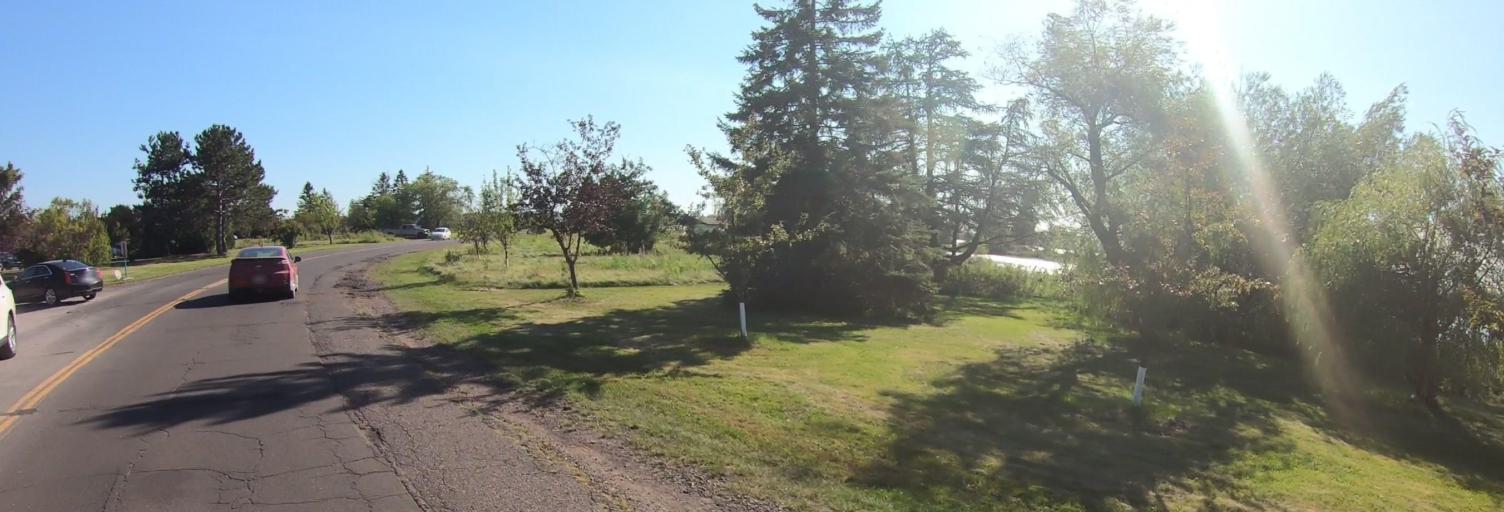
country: US
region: Wisconsin
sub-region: Douglas County
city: Superior
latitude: 46.7325
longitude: -92.0538
